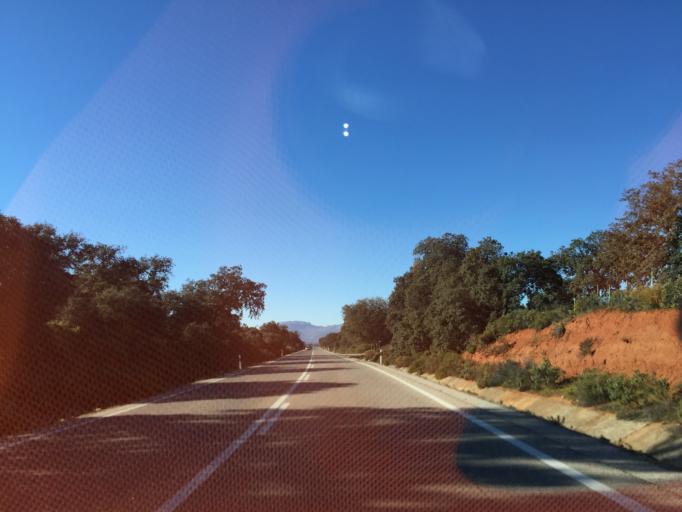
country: ES
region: Andalusia
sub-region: Provincia de Malaga
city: Arriate
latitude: 36.8229
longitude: -5.0960
